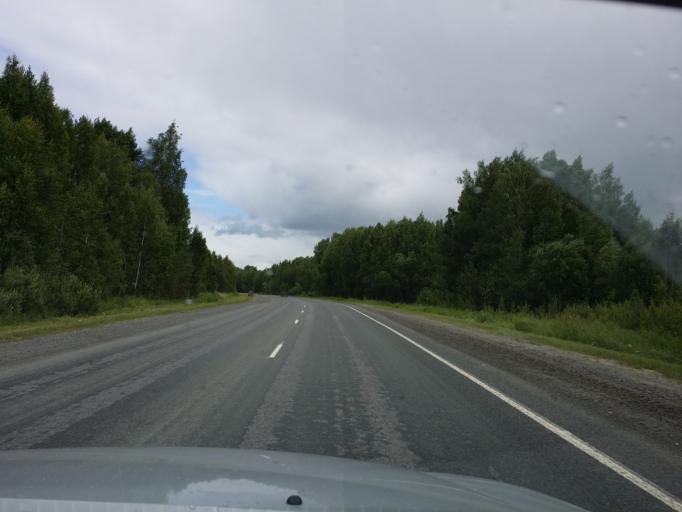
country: RU
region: Tjumen
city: Abalak
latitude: 58.4819
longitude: 68.6332
